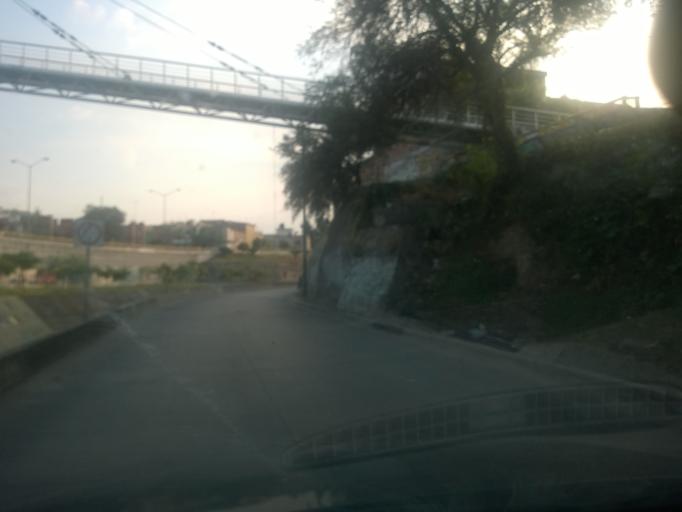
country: MX
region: Guanajuato
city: Leon
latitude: 21.1449
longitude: -101.6795
